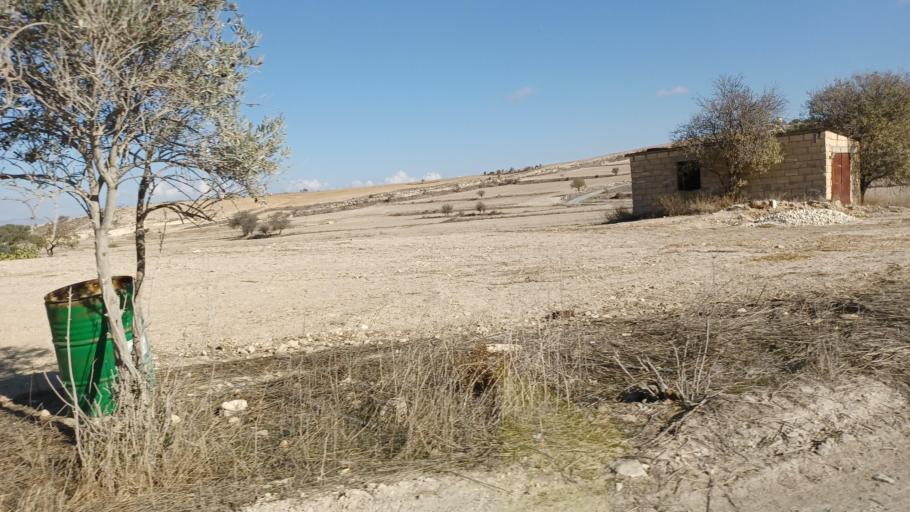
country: CY
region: Larnaka
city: Troulloi
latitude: 35.0343
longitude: 33.5741
